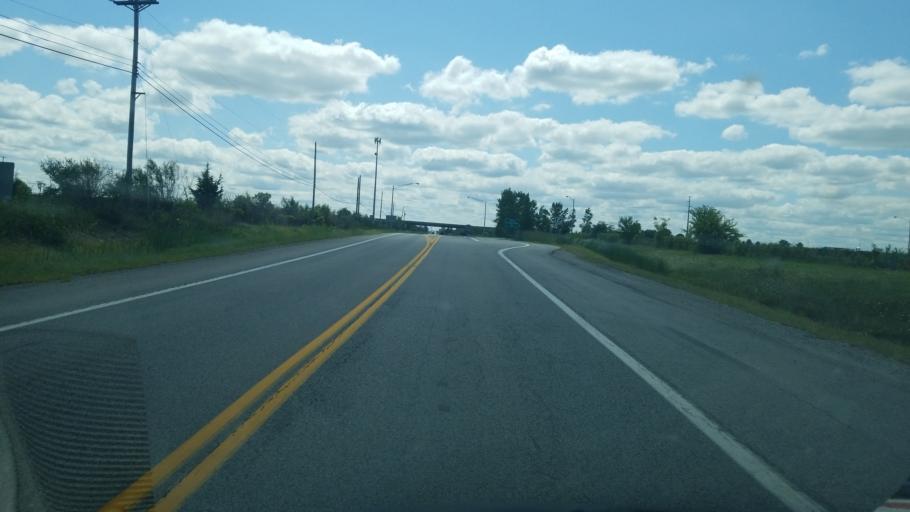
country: US
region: Ohio
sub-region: Fulton County
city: Delta
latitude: 41.5956
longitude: -84.0376
